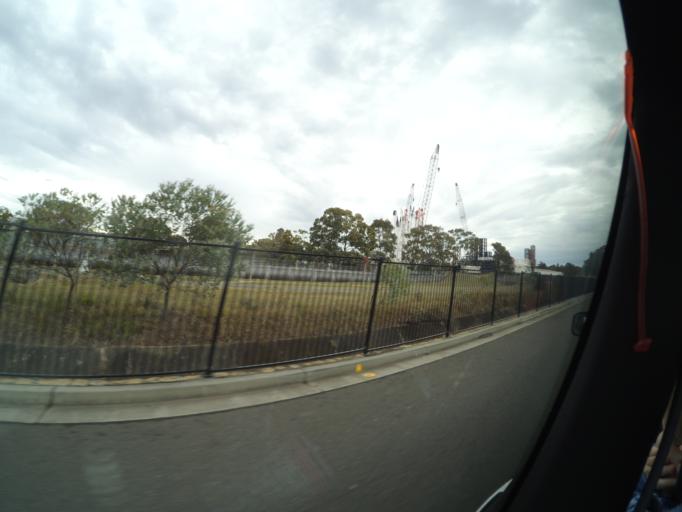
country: AU
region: New South Wales
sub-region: Bankstown
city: Regents Park
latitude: -33.8798
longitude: 151.0163
